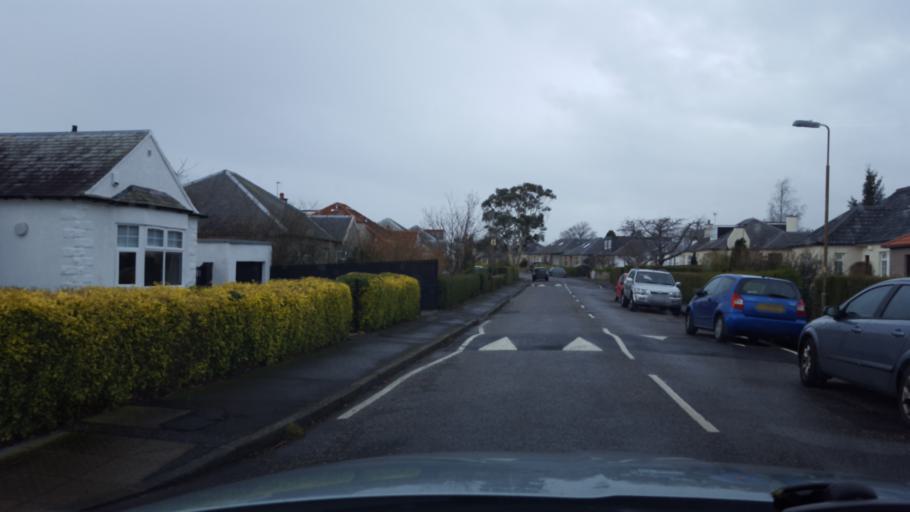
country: GB
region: Scotland
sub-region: Edinburgh
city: Colinton
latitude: 55.9062
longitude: -3.2817
